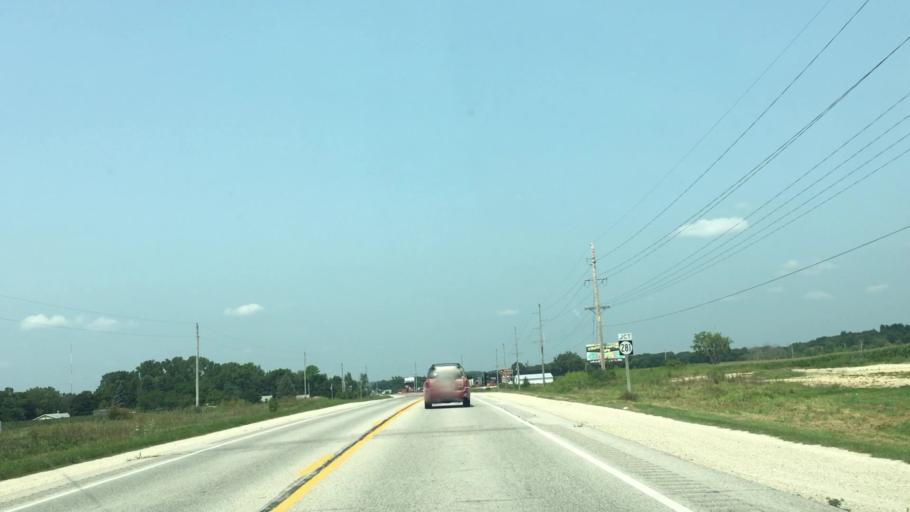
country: US
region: Iowa
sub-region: Fayette County
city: Oelwein
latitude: 42.6377
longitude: -91.9086
